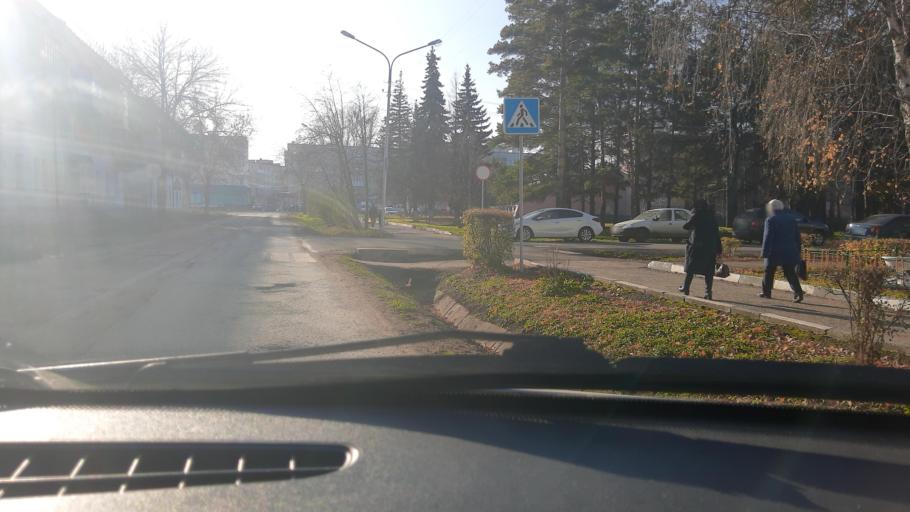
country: RU
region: Bashkortostan
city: Mikhaylovka
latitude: 54.7055
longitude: 55.8374
